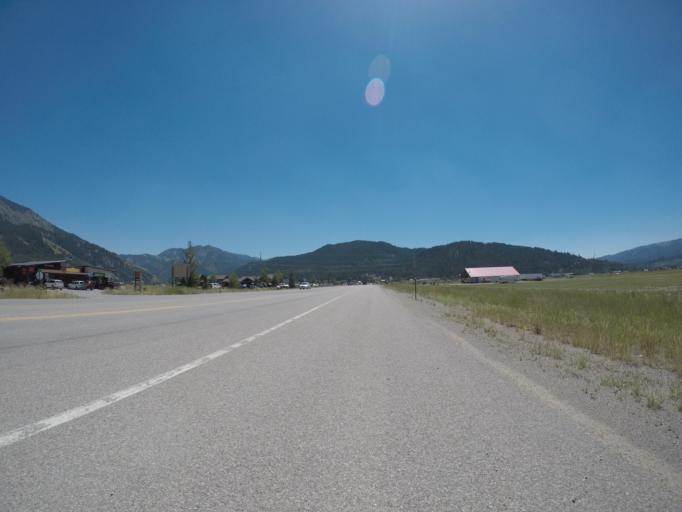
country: US
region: Wyoming
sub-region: Teton County
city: Hoback
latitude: 43.1706
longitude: -111.0183
